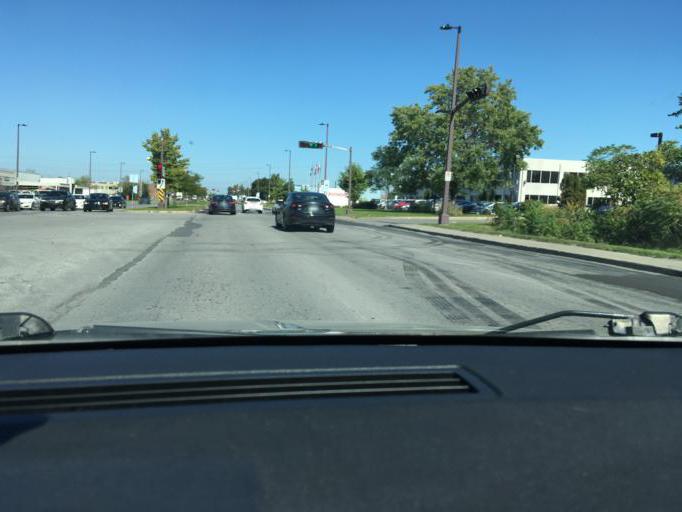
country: CA
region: Quebec
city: Dorval
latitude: 45.5030
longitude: -73.7437
